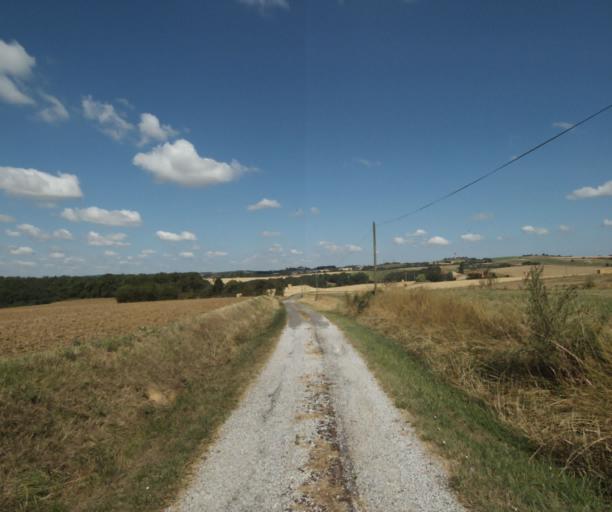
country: FR
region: Midi-Pyrenees
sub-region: Departement de la Haute-Garonne
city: Auriac-sur-Vendinelle
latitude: 43.4514
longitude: 1.7857
